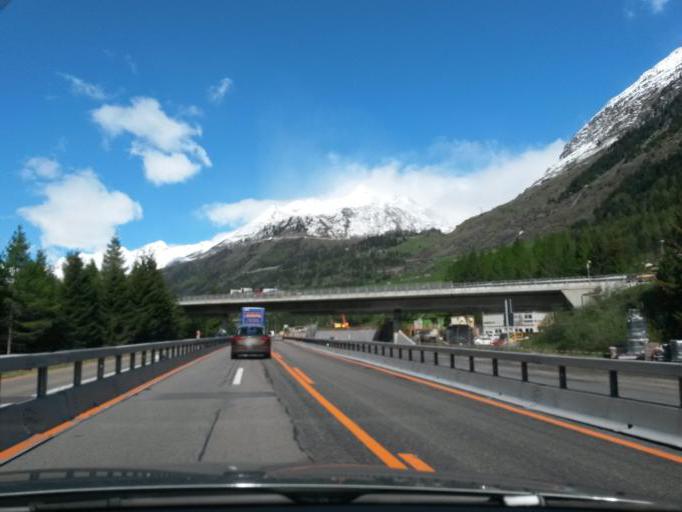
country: CH
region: Ticino
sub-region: Leventina District
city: Airolo
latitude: 46.5262
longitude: 8.6127
